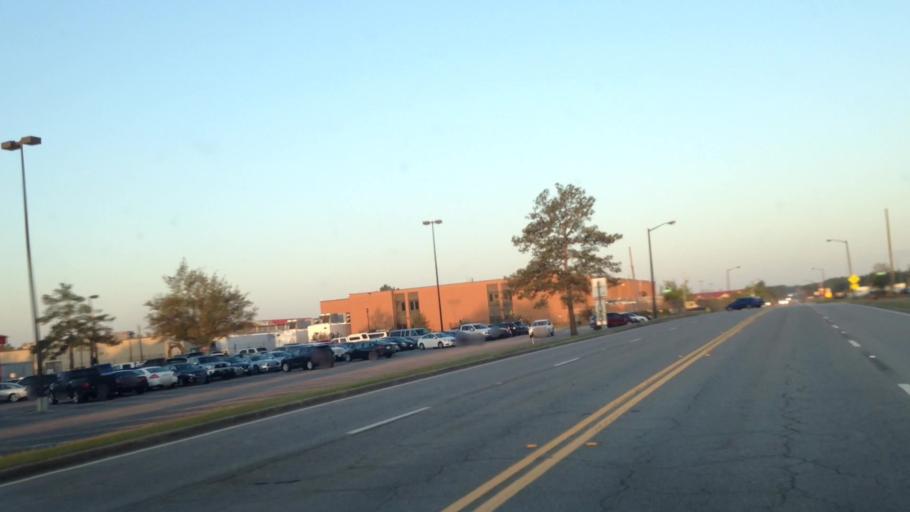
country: US
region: Georgia
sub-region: Columbia County
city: Grovetown
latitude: 33.4255
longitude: -82.1510
